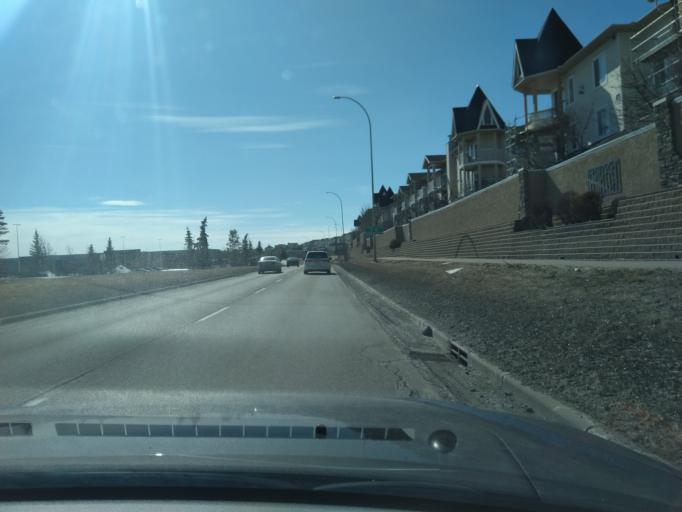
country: CA
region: Alberta
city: Calgary
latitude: 51.1590
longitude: -114.0708
